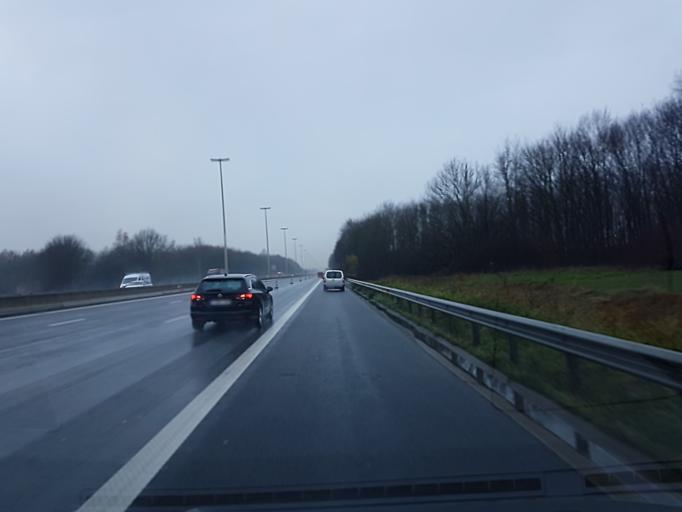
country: BE
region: Wallonia
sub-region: Province de Liege
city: Heron
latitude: 50.5300
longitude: 5.0759
